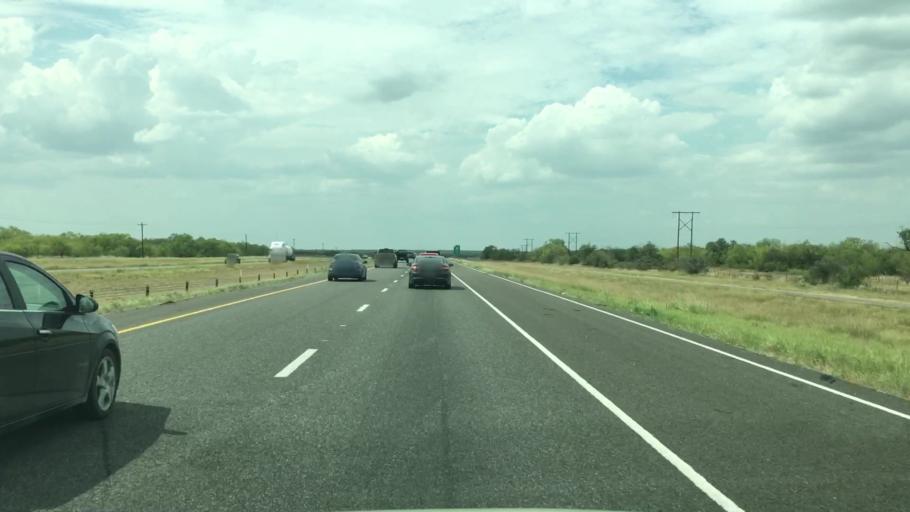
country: US
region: Texas
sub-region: Atascosa County
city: Pleasanton
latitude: 28.8244
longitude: -98.3641
